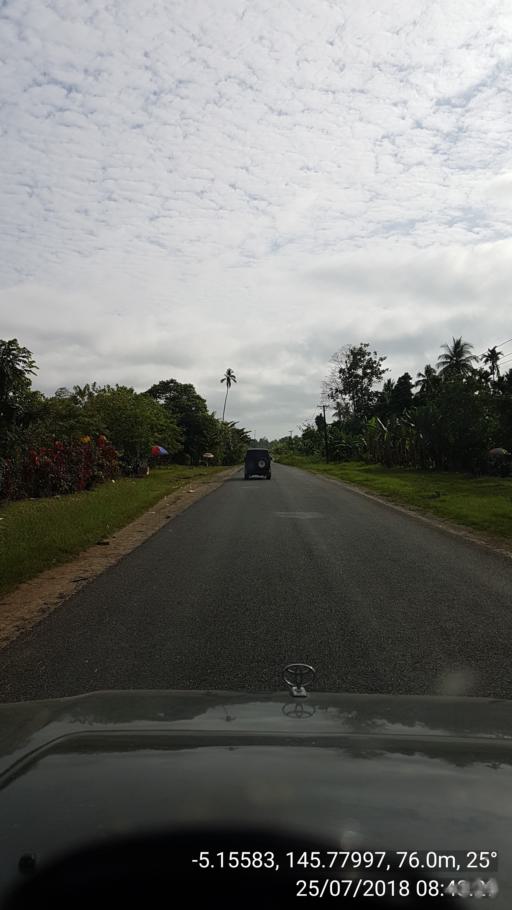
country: PG
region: Madang
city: Madang
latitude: -5.1569
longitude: 145.7795
